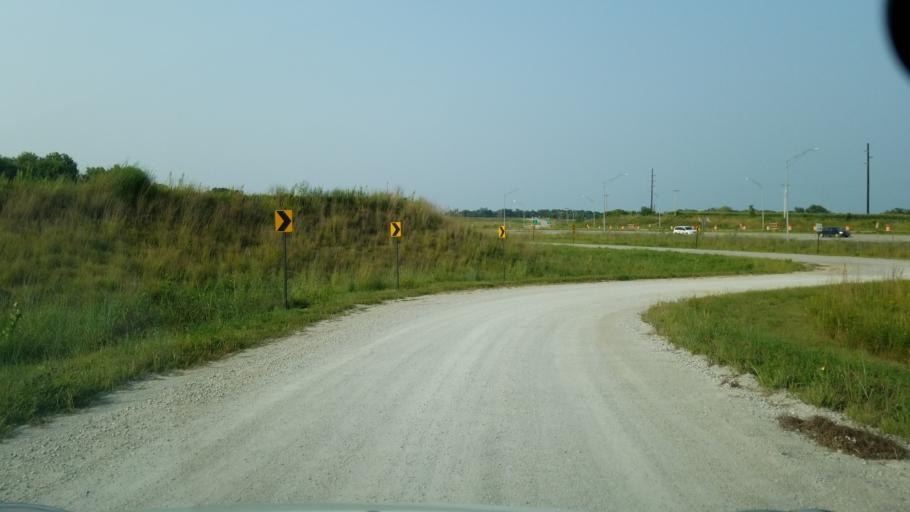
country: US
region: Nebraska
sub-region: Sarpy County
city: Offutt Air Force Base
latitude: 41.0760
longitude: -95.9293
